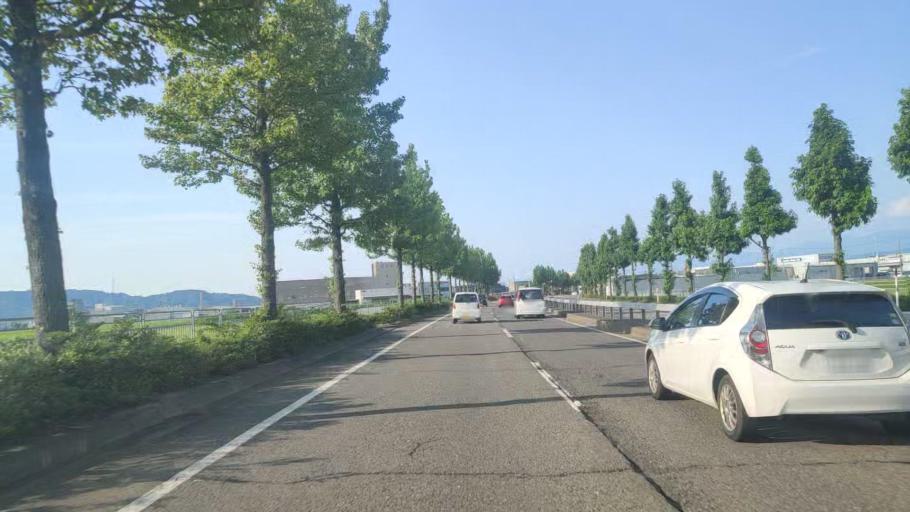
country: JP
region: Fukui
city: Fukui-shi
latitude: 36.0164
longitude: 136.2104
